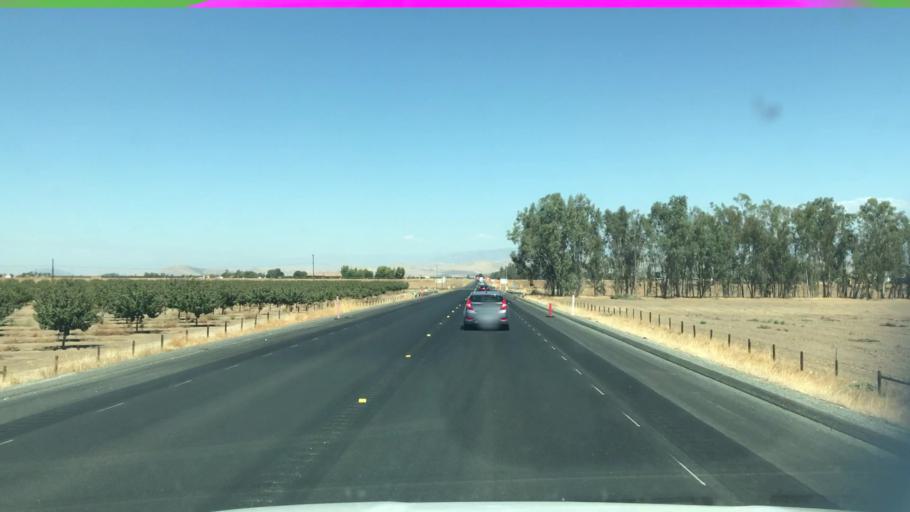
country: US
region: California
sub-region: Tulare County
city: Terra Bella
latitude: 35.9901
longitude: -119.0490
